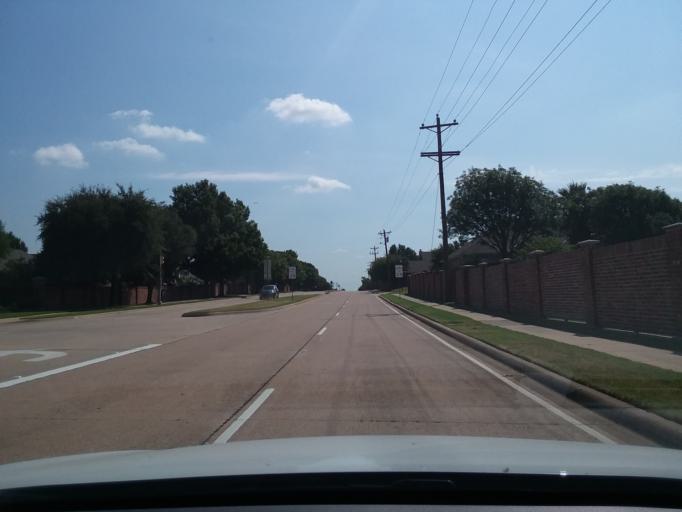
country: US
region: Texas
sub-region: Denton County
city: Lewisville
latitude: 33.0207
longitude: -97.0402
